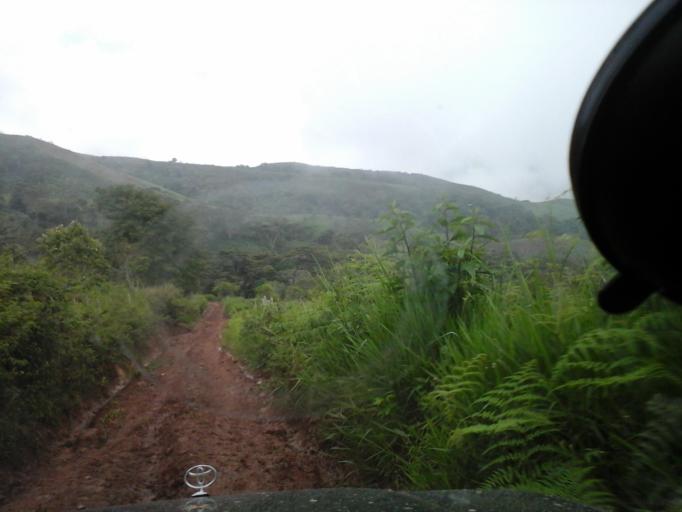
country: CO
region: Cesar
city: Agustin Codazzi
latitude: 9.9602
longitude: -73.0622
